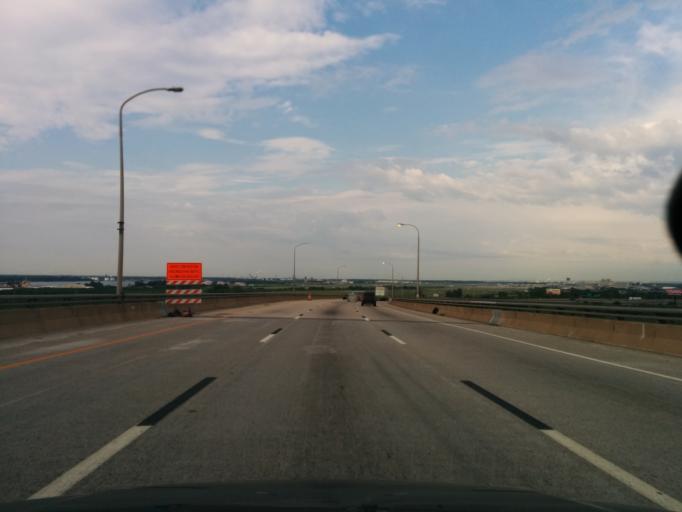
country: US
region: New Jersey
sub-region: Gloucester County
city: National Park
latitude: 39.8882
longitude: -75.2032
